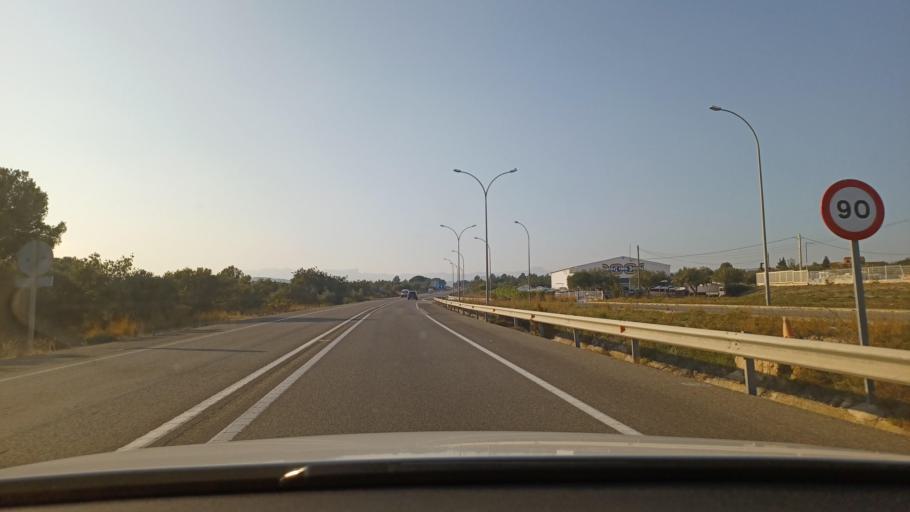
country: ES
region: Catalonia
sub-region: Provincia de Tarragona
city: l'Ametlla de Mar
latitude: 40.8933
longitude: 0.7807
